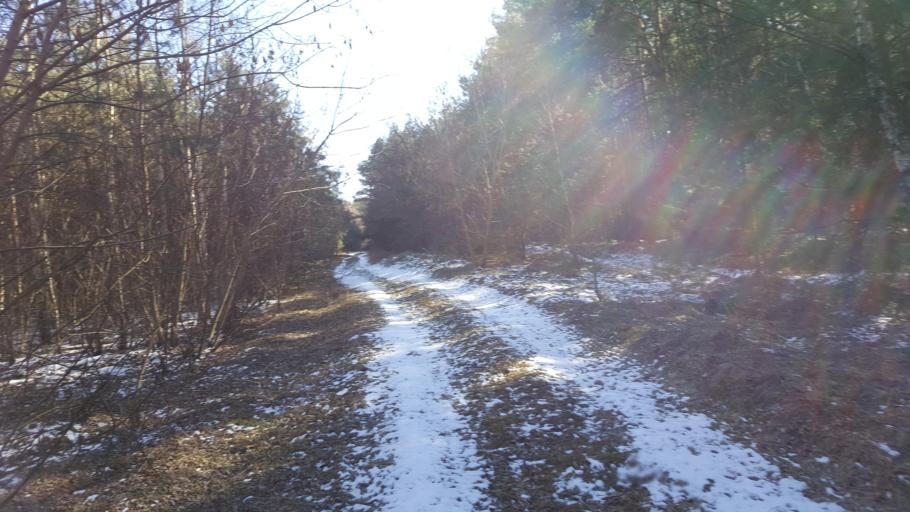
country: BY
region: Brest
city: Kamyanyets
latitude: 52.3687
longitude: 23.8160
